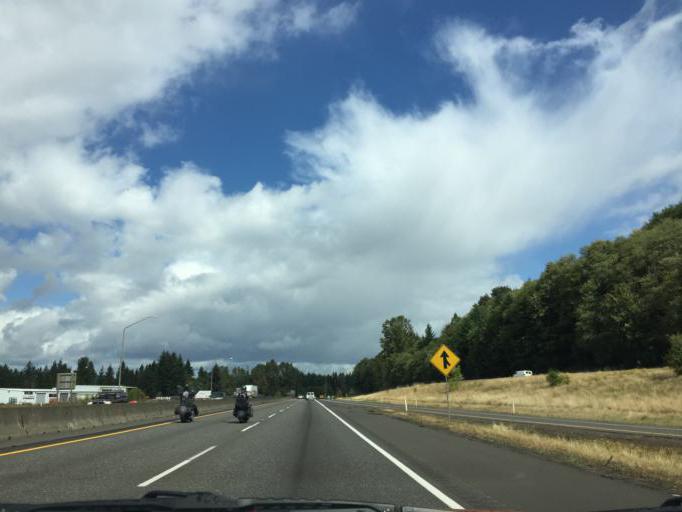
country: US
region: Washington
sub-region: Lewis County
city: Winlock
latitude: 46.3931
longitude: -122.9010
